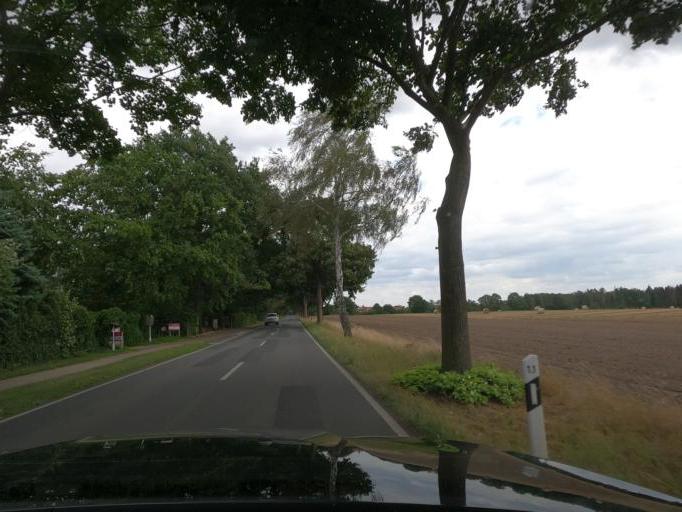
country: DE
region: Lower Saxony
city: Isernhagen Farster Bauerschaft
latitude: 52.4692
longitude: 9.8777
